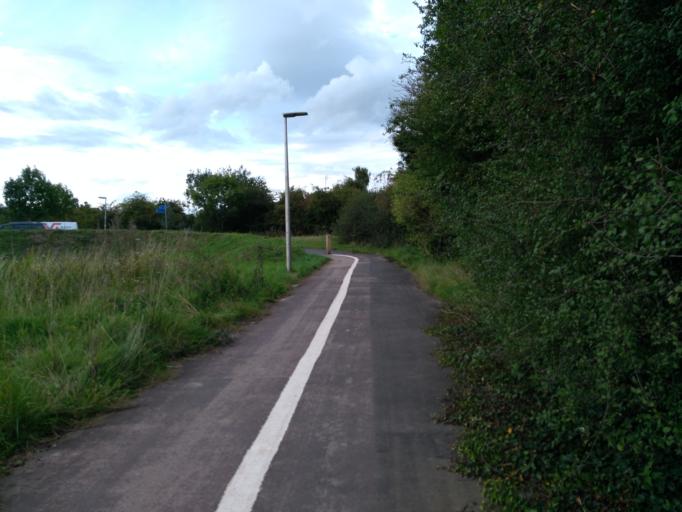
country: GB
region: England
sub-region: Central Bedfordshire
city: Houghton Regis
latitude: 51.9052
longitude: -0.4986
